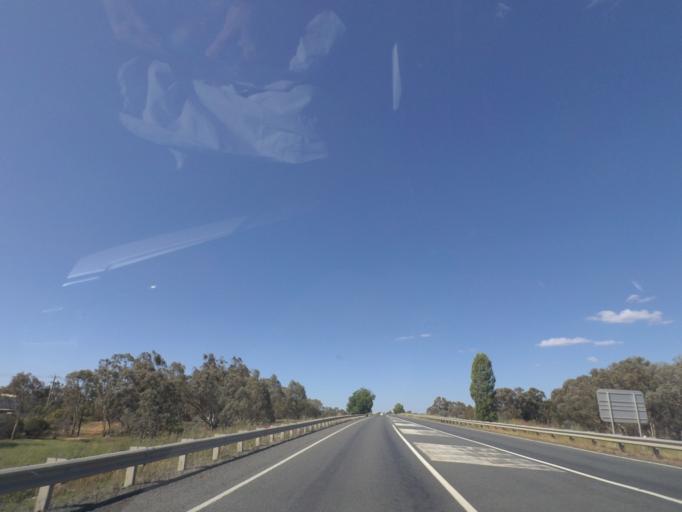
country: AU
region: New South Wales
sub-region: Albury Municipality
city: Lavington
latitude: -36.0039
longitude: 146.9871
